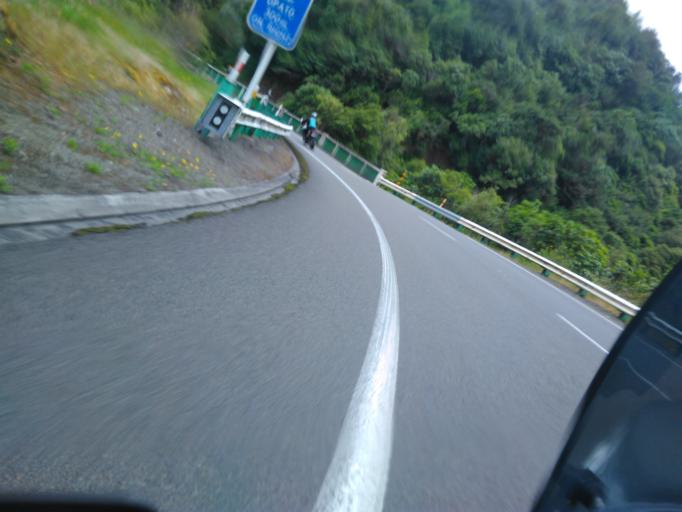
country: NZ
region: Bay of Plenty
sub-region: Opotiki District
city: Opotiki
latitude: -38.3389
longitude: 177.4223
